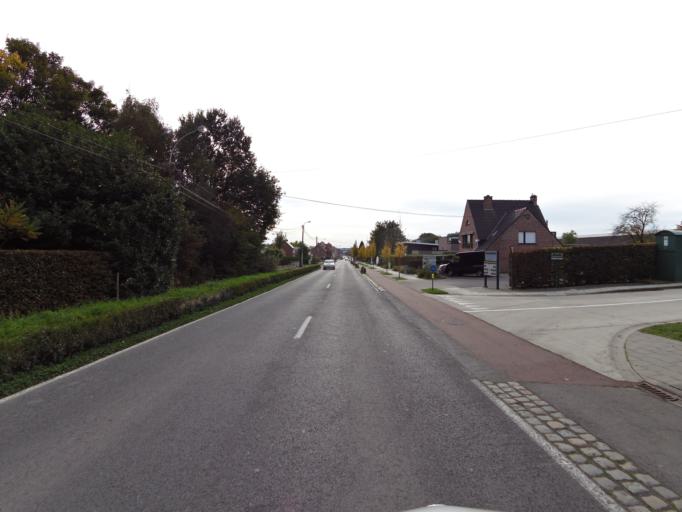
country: BE
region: Flanders
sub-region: Provincie West-Vlaanderen
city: Torhout
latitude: 51.0767
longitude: 3.0982
